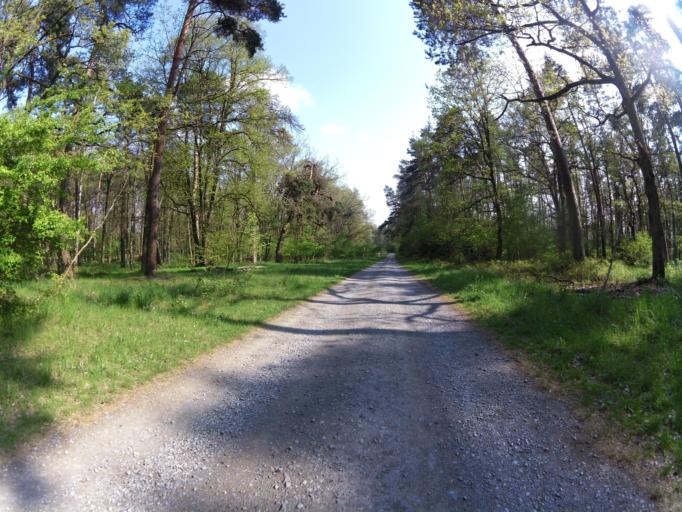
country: DE
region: Bavaria
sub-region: Regierungsbezirk Unterfranken
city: Sommerhausen
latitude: 49.7037
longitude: 10.0533
